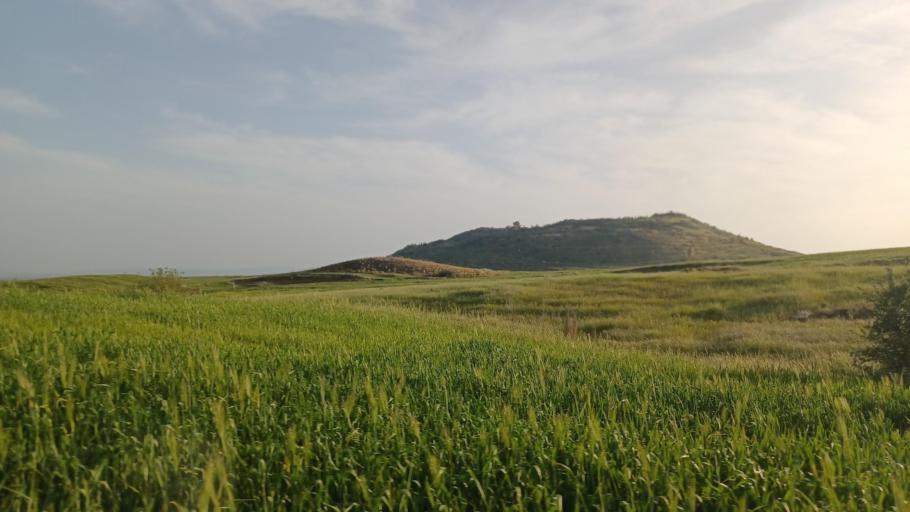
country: CY
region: Lefkosia
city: Lefka
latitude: 35.0840
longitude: 32.9494
